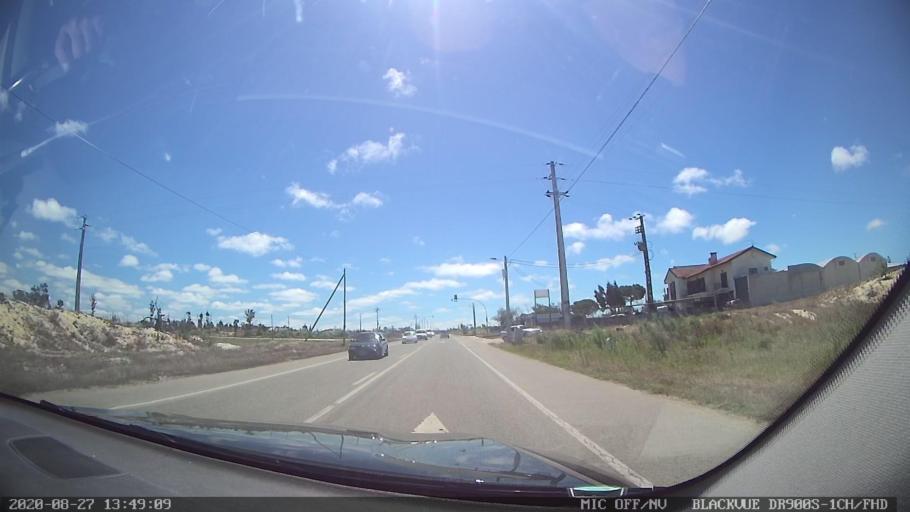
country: PT
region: Coimbra
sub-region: Mira
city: Mira
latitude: 40.3701
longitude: -8.7459
